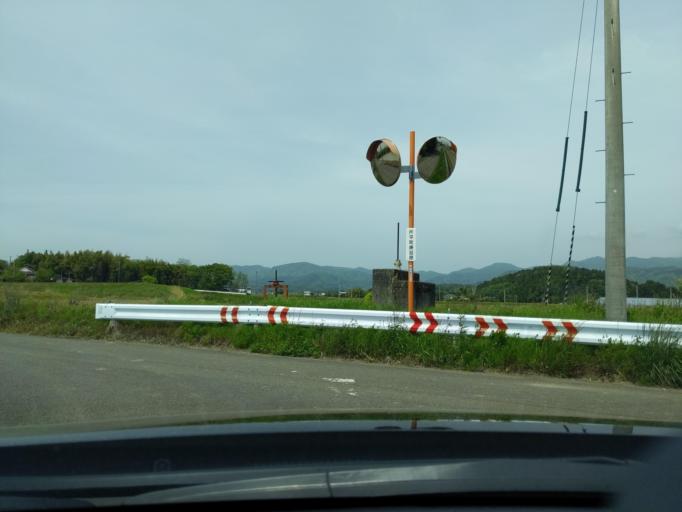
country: JP
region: Fukushima
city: Koriyama
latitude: 37.4050
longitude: 140.2980
